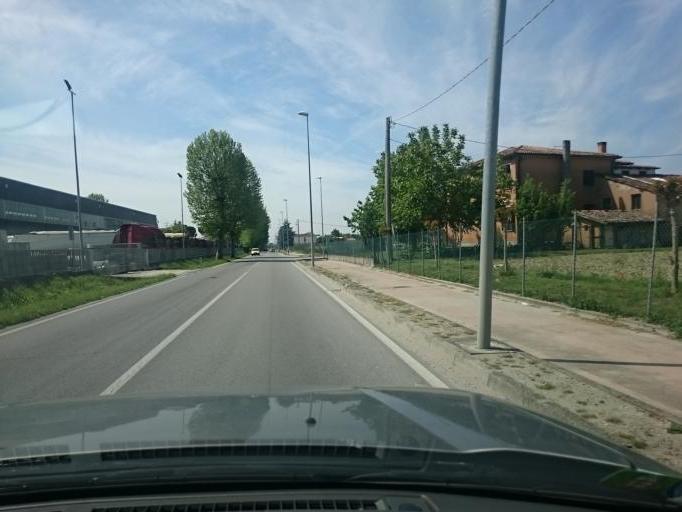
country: IT
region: Veneto
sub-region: Provincia di Padova
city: Cartura
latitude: 45.2602
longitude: 11.8609
